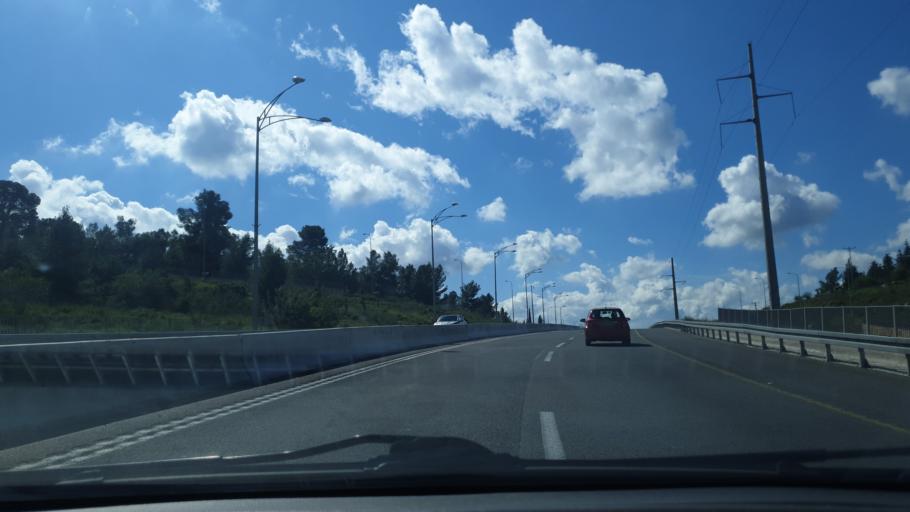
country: IL
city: Mevo horon
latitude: 31.8142
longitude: 35.0222
